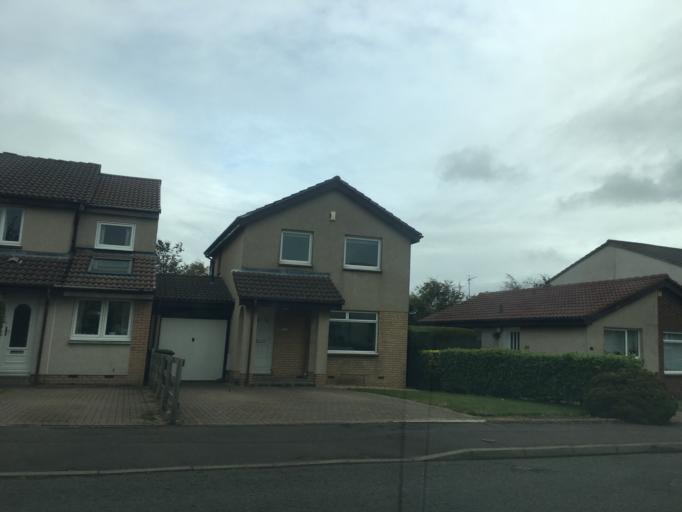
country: GB
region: Scotland
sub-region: Edinburgh
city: Colinton
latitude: 55.9008
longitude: -3.2219
